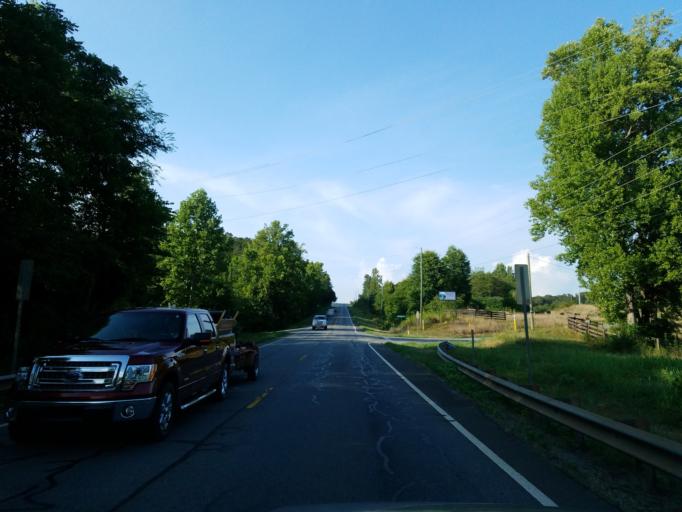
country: US
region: Georgia
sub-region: Bartow County
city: Rydal
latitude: 34.3697
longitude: -84.7124
